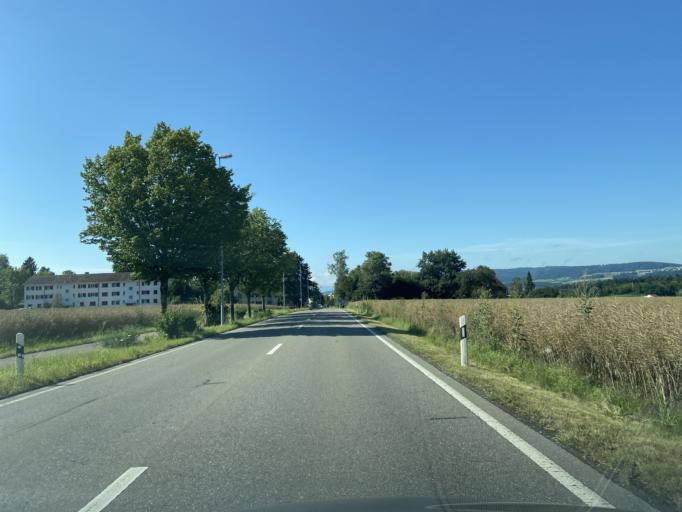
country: CH
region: Zurich
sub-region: Bezirk Uster
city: Uster / Gschwader
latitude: 47.3642
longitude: 8.7111
